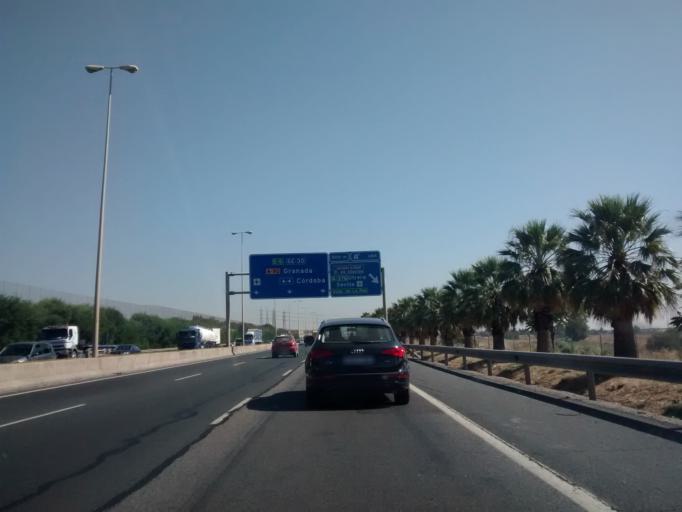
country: ES
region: Andalusia
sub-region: Provincia de Sevilla
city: Sevilla
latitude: 37.3518
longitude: -5.9605
